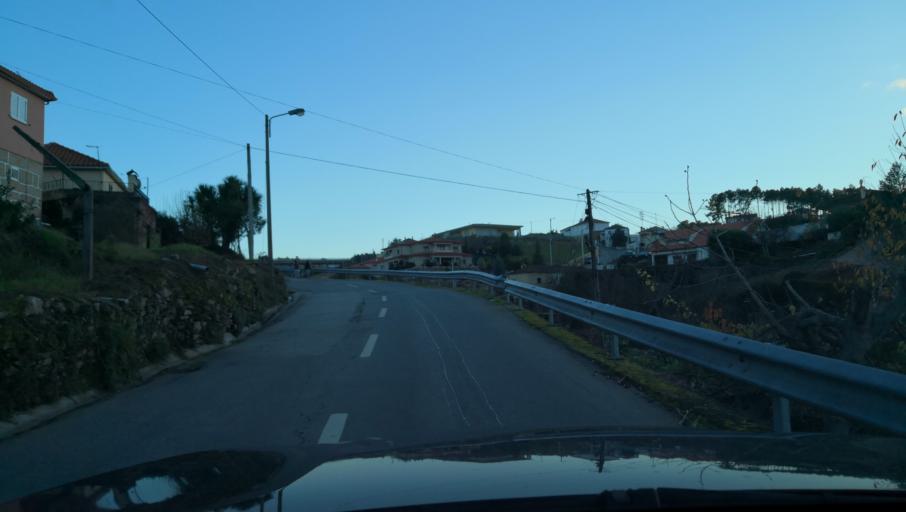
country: PT
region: Vila Real
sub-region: Vila Real
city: Vila Real
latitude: 41.2884
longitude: -7.7179
